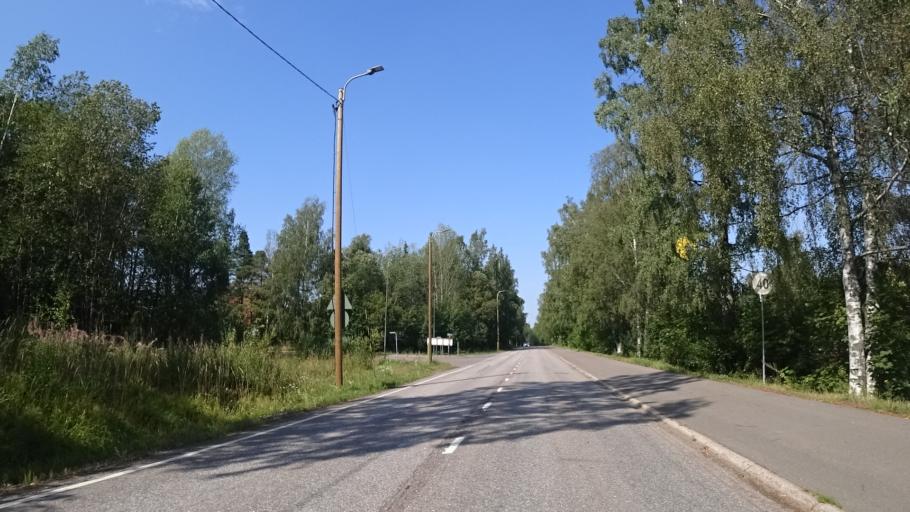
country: FI
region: Kymenlaakso
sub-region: Kotka-Hamina
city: Karhula
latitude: 60.5019
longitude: 26.9526
